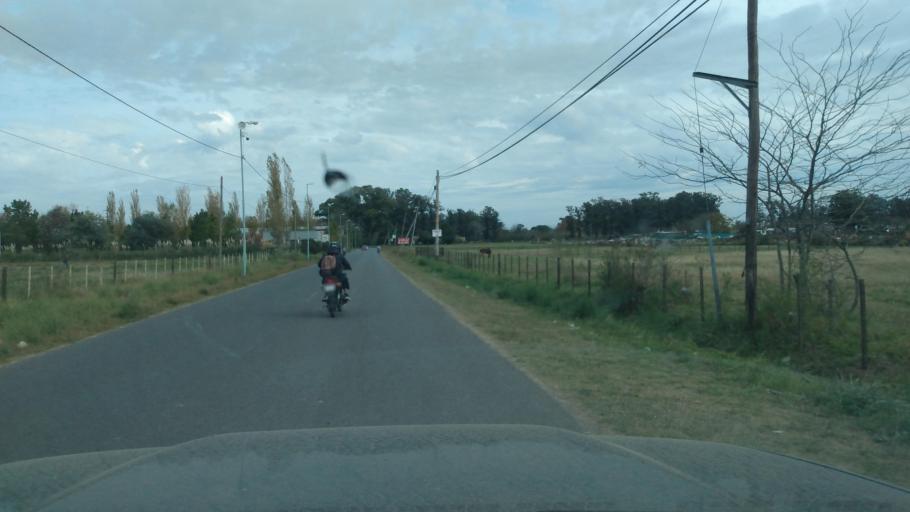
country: AR
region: Buenos Aires
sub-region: Partido de Lujan
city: Lujan
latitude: -34.5825
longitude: -59.1249
